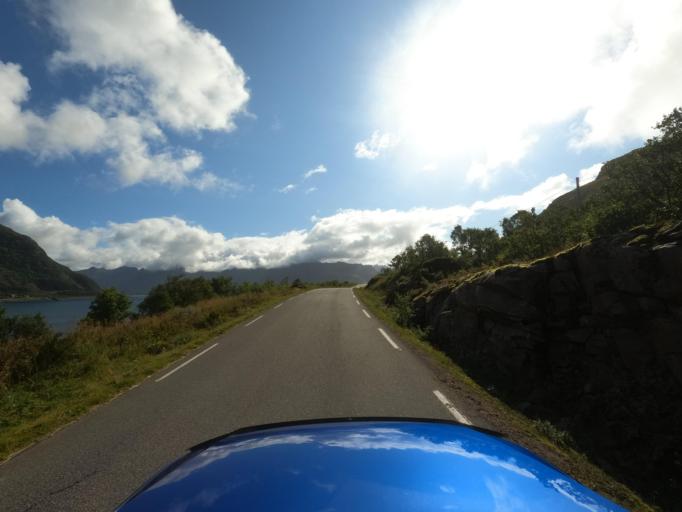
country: NO
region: Nordland
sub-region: Vagan
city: Kabelvag
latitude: 68.2639
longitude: 14.1598
